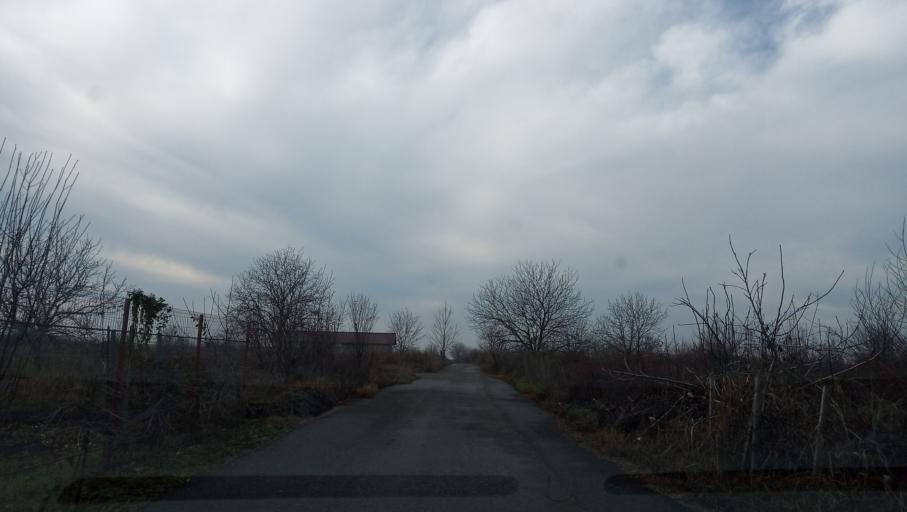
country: RO
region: Giurgiu
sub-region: Comuna Herasti
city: Herasti
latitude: 44.2203
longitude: 26.3551
